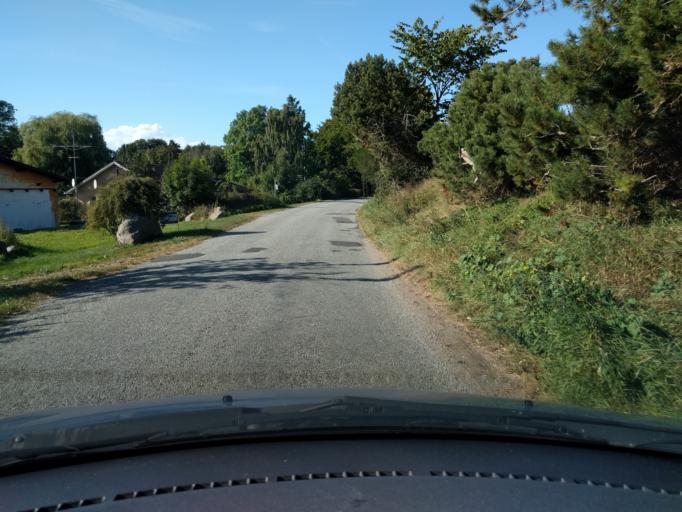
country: DK
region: South Denmark
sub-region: Assens Kommune
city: Harby
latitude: 55.1388
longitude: 10.0249
